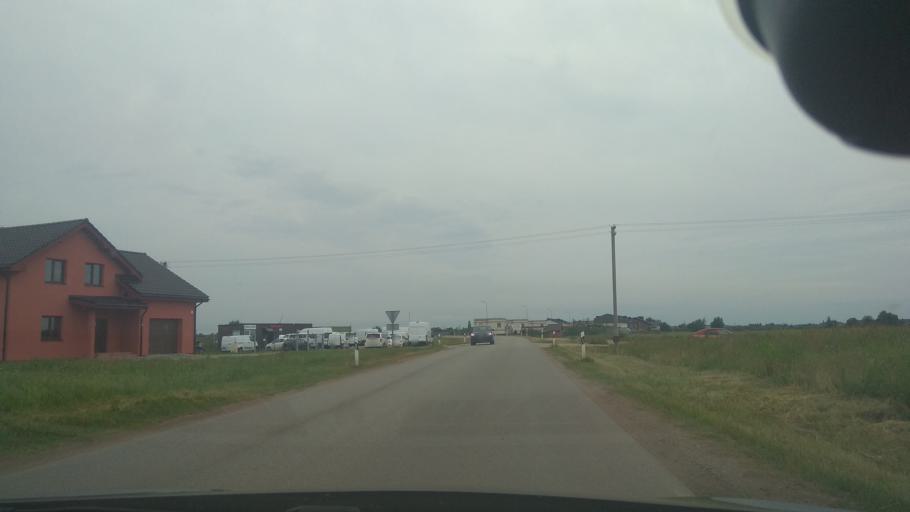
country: LT
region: Klaipedos apskritis
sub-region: Klaipeda
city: Klaipeda
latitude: 55.7536
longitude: 21.1747
